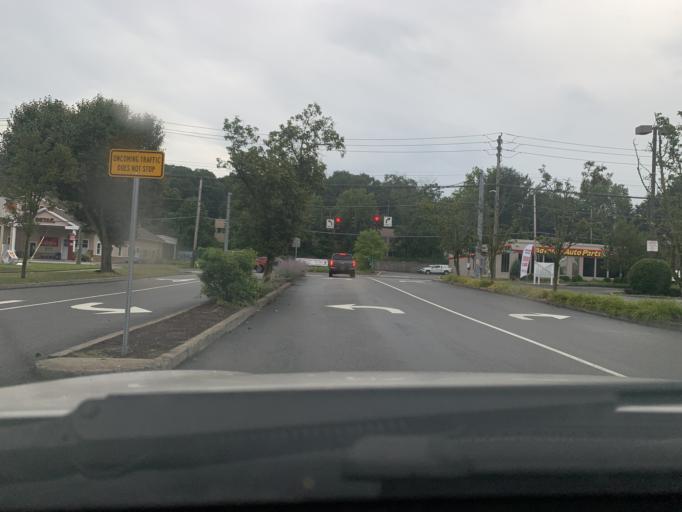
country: US
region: New York
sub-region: Westchester County
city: Ossining
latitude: 41.1447
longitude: -73.8617
